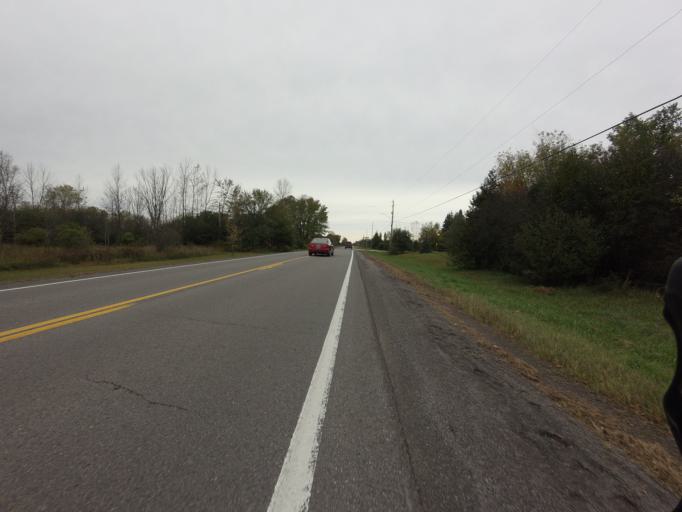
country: CA
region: Ontario
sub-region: Lanark County
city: Smiths Falls
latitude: 44.8655
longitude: -75.8082
